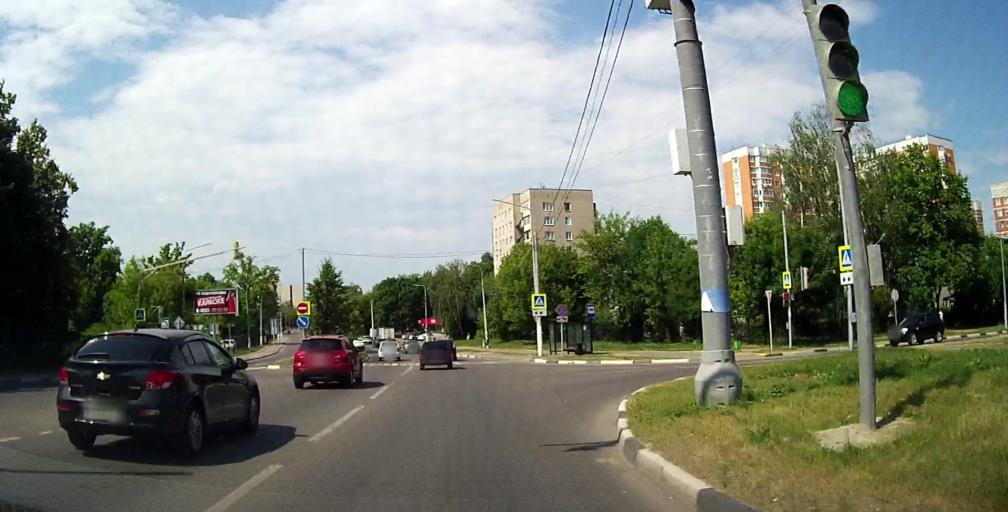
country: RU
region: Moskovskaya
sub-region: Podol'skiy Rayon
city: Podol'sk
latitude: 55.4185
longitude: 37.5198
